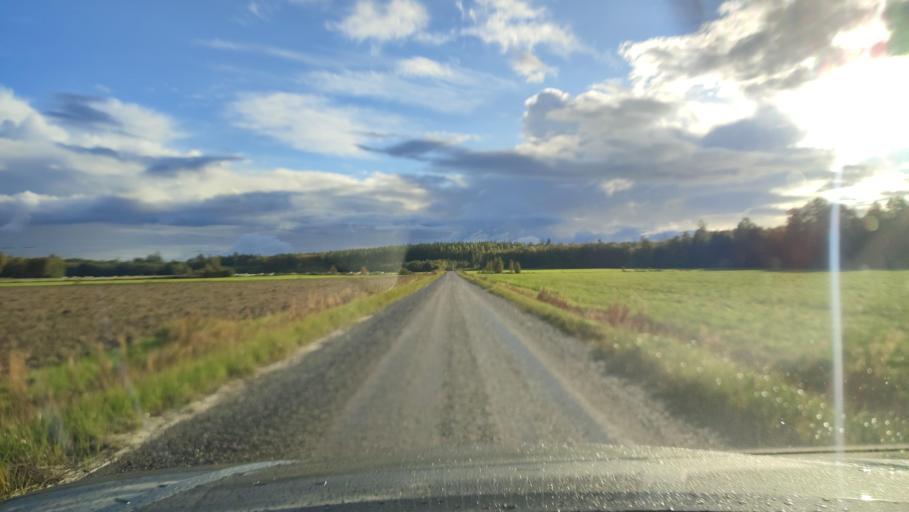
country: FI
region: Southern Ostrobothnia
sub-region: Suupohja
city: Karijoki
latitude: 62.3122
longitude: 21.5507
